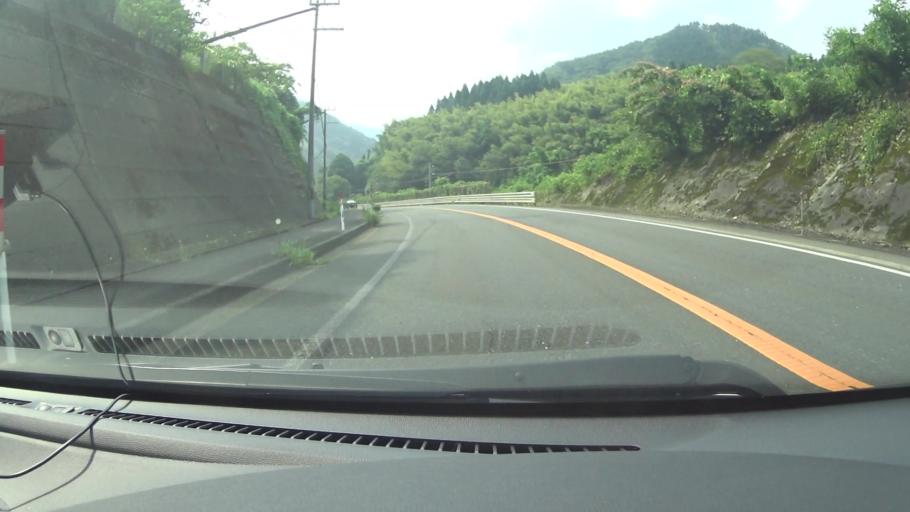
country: JP
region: Kyoto
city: Maizuru
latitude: 35.4739
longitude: 135.3852
